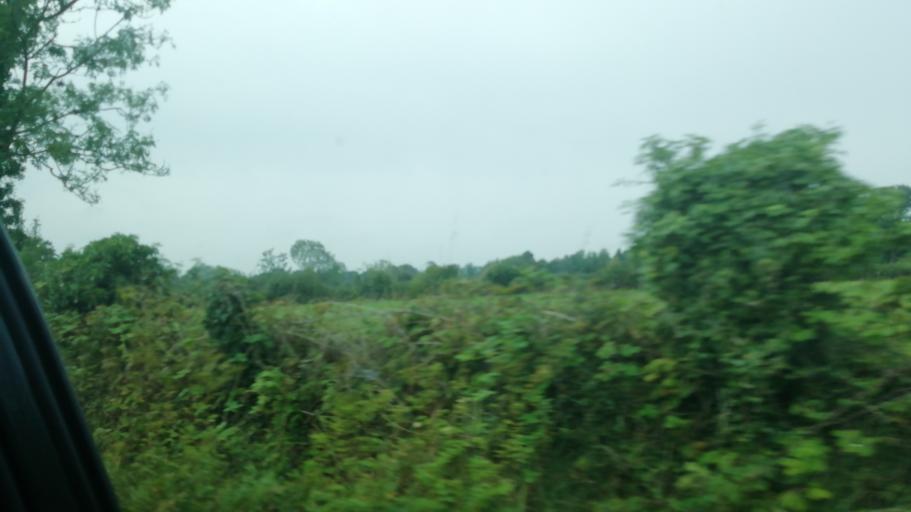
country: IE
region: Leinster
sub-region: Kilkenny
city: Callan
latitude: 52.5378
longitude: -7.5221
